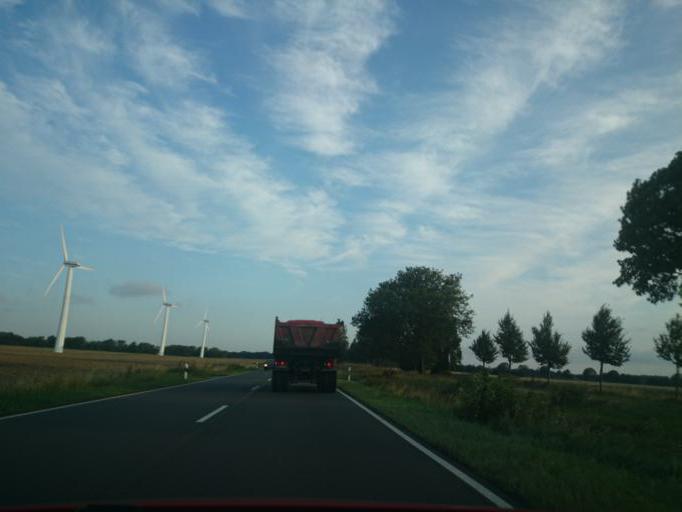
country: DE
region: Mecklenburg-Vorpommern
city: Mesekenhagen
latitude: 54.1870
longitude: 13.2790
